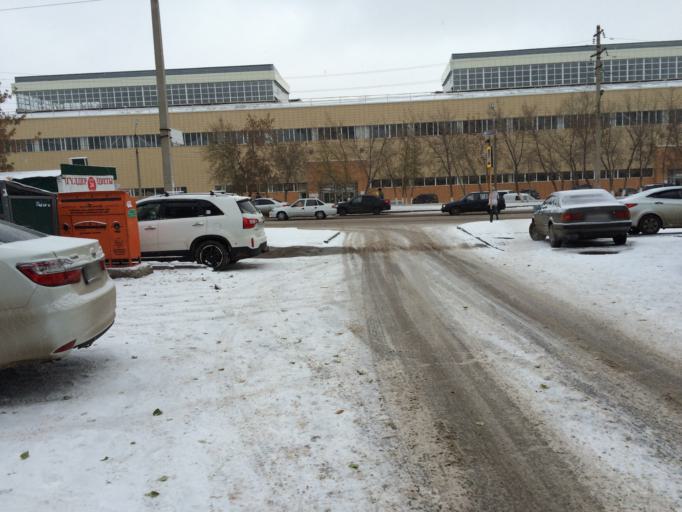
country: KZ
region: Astana Qalasy
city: Astana
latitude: 51.1803
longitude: 71.4337
